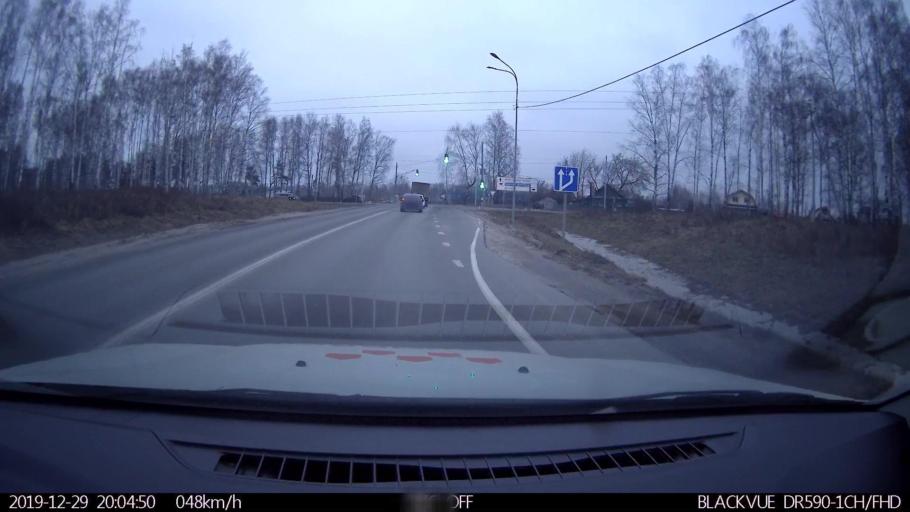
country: RU
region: Nizjnij Novgorod
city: Neklyudovo
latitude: 56.3876
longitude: 44.0100
